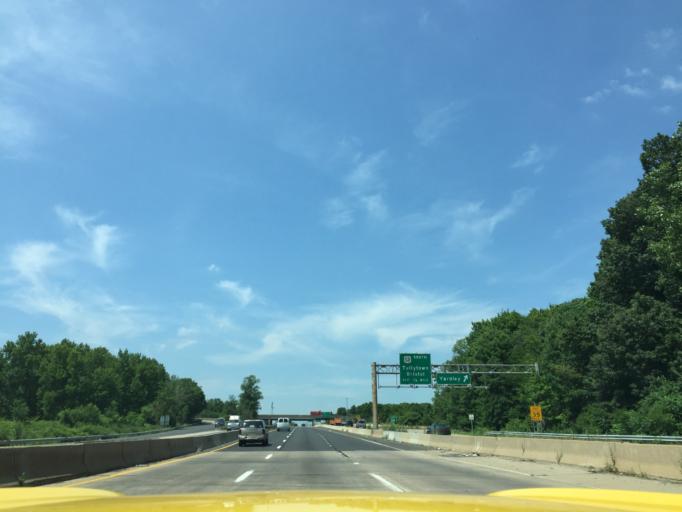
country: US
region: Pennsylvania
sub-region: Bucks County
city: Morrisville
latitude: 40.1972
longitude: -74.7977
